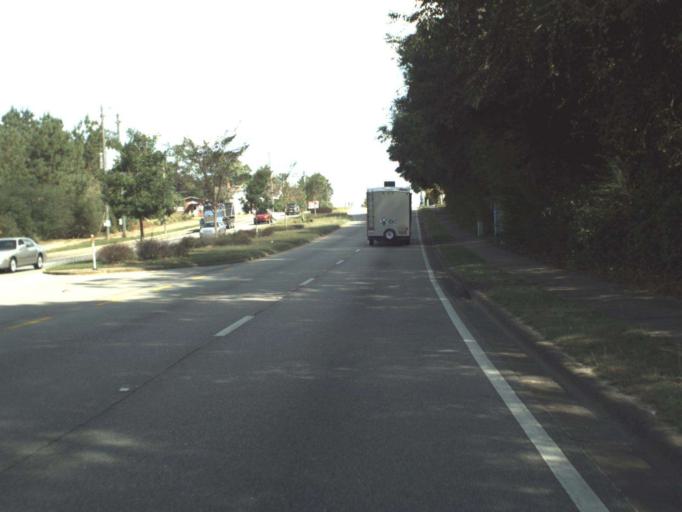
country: US
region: Florida
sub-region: Walton County
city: DeFuniak Springs
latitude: 30.7170
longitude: -86.1222
